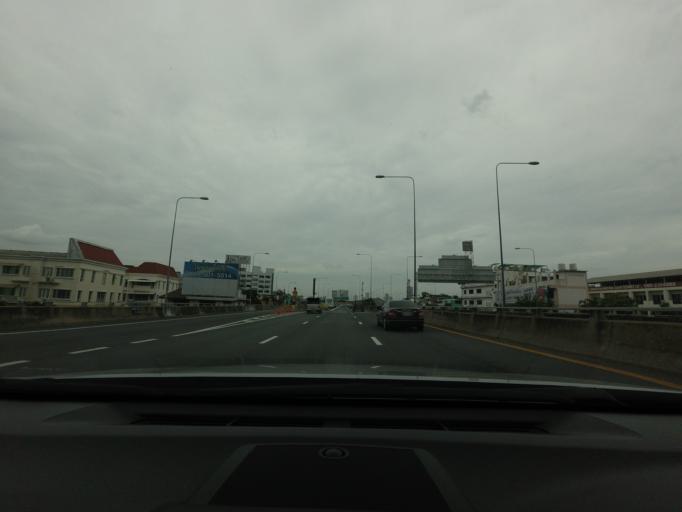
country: TH
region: Bangkok
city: Sathon
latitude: 13.6963
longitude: 100.5239
